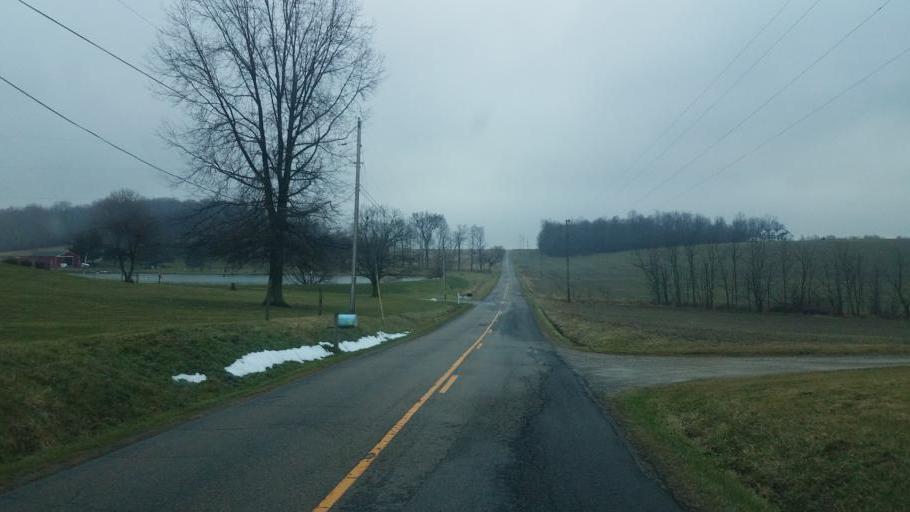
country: US
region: Ohio
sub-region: Sandusky County
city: Bellville
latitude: 40.5370
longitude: -82.3960
